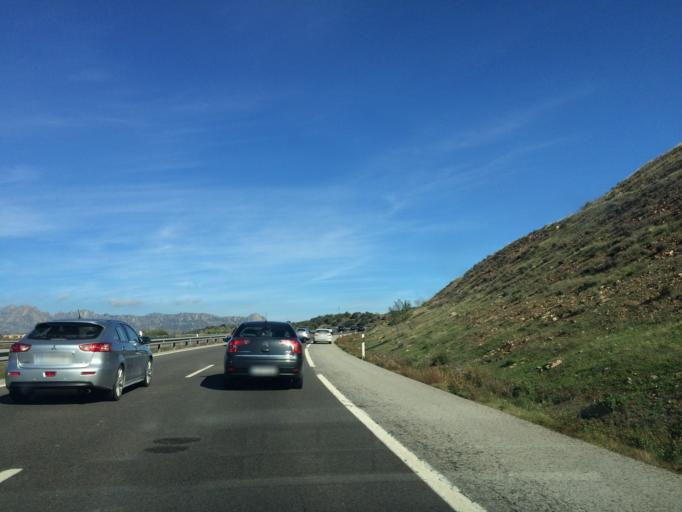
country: ES
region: Madrid
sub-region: Provincia de Madrid
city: Venturada
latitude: 40.8081
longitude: -3.6198
